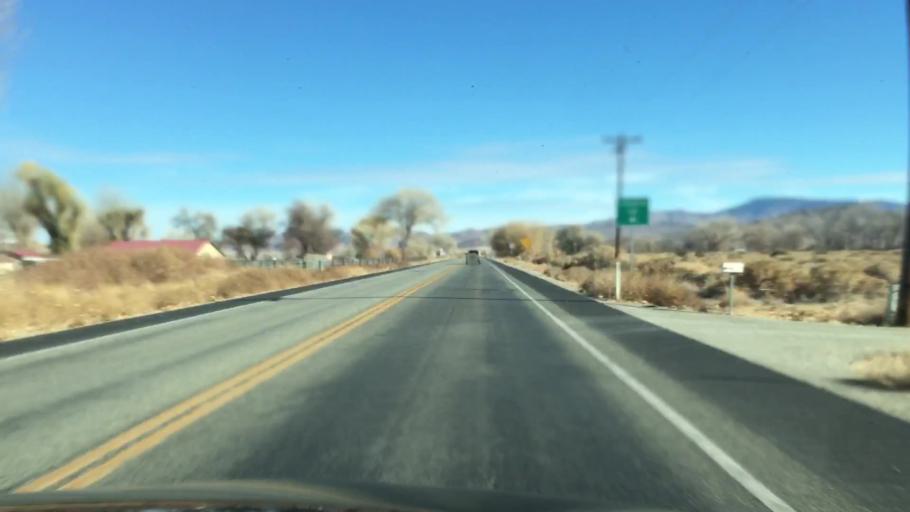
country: US
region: Nevada
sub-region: Lyon County
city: Yerington
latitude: 38.9976
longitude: -119.1441
